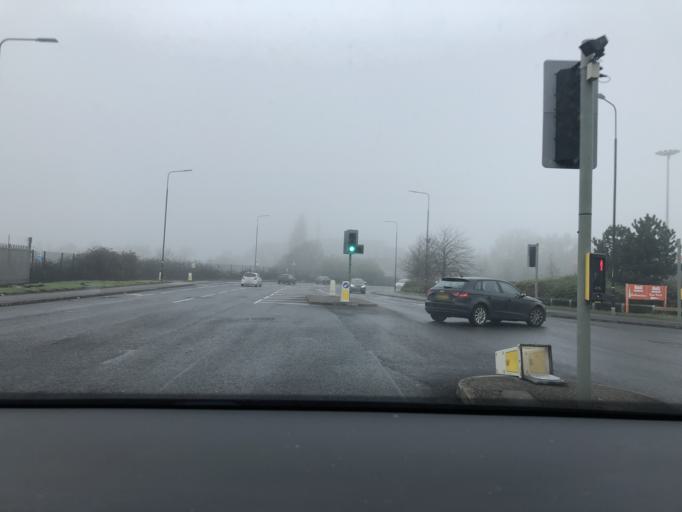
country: GB
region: England
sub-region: City and Borough of Salford
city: Eccles
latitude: 53.4716
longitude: -2.3511
